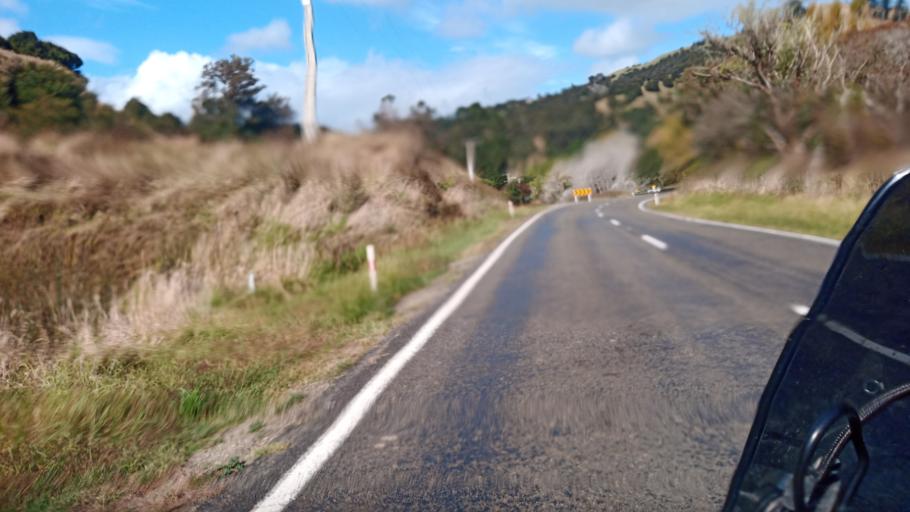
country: NZ
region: Gisborne
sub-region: Gisborne District
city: Gisborne
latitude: -38.4679
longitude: 177.6642
